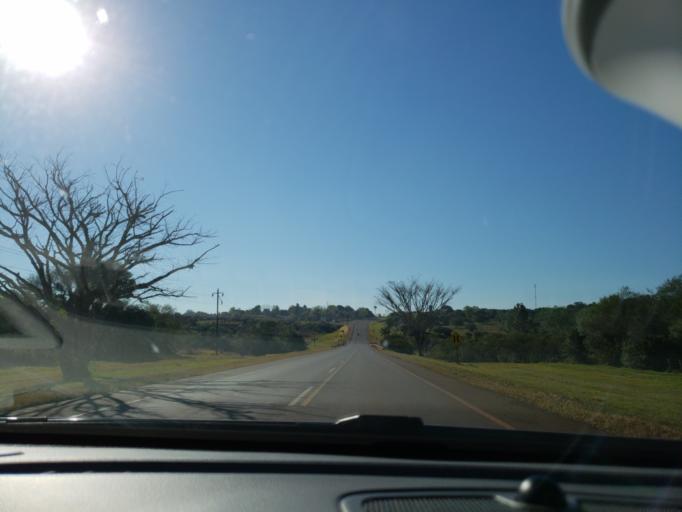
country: AR
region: Misiones
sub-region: Departamento de Apostoles
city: San Jose
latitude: -27.7793
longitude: -55.7730
